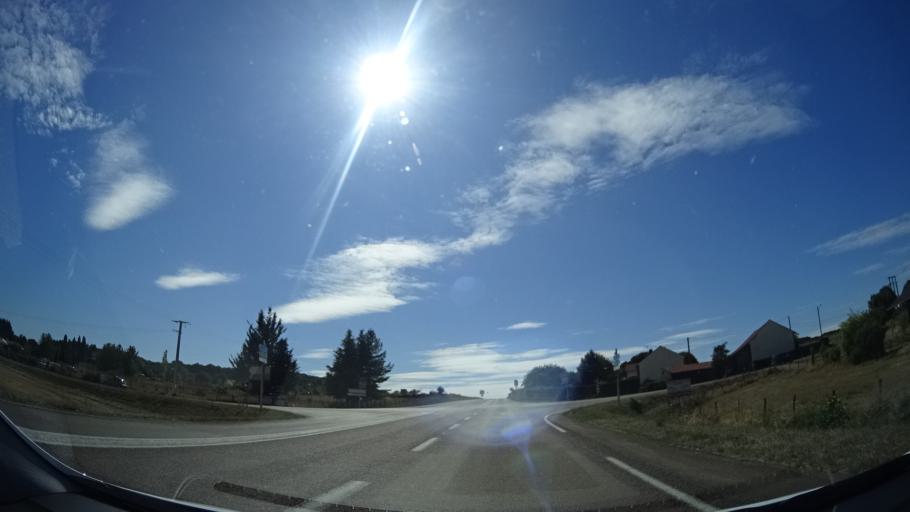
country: FR
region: Bourgogne
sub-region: Departement de l'Yonne
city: Saint-Julien-du-Sault
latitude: 47.9377
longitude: 3.2393
